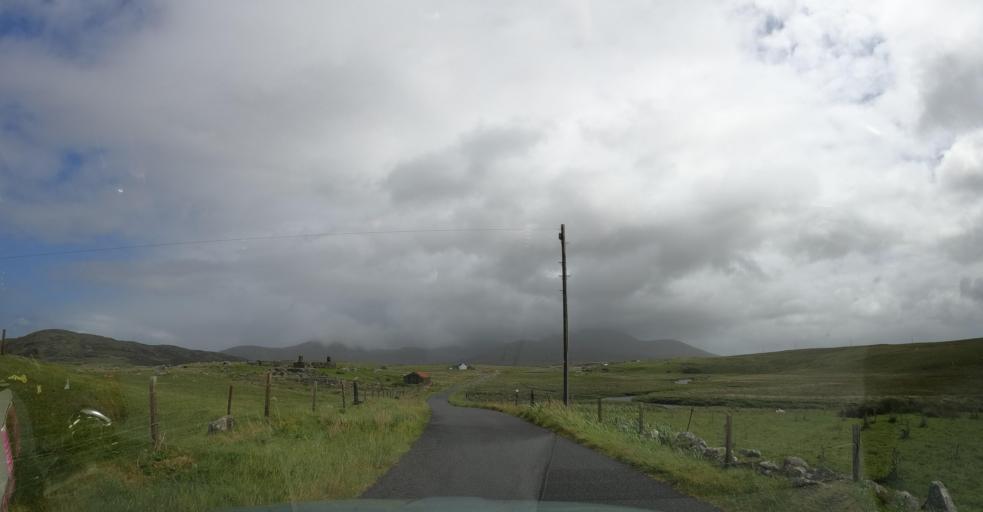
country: GB
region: Scotland
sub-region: Eilean Siar
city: Isle of South Uist
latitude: 57.2912
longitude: -7.3758
